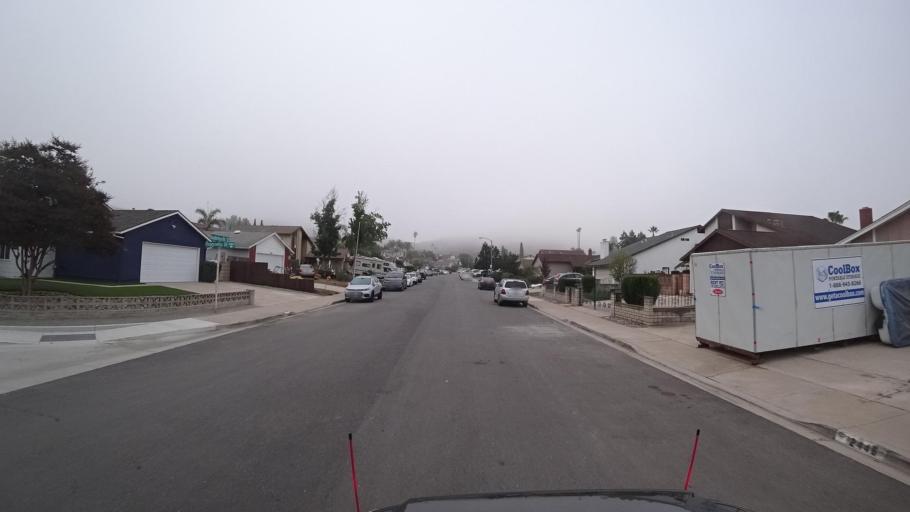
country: US
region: California
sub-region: San Diego County
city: Rancho San Diego
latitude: 32.7288
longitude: -116.9591
